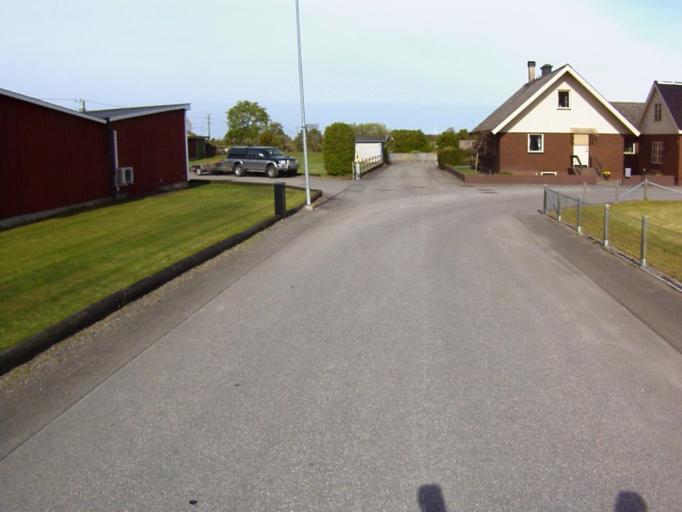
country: SE
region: Skane
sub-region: Kristianstads Kommun
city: Fjalkinge
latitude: 56.0452
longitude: 14.2741
